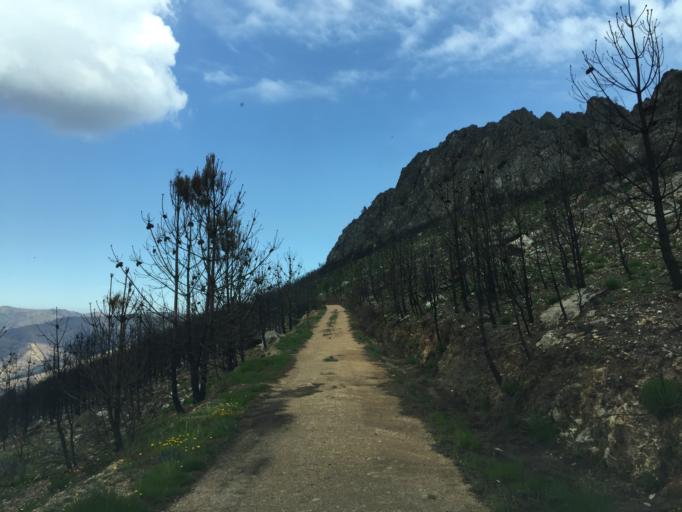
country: PT
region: Coimbra
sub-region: Pampilhosa da Serra
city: Pampilhosa da Serra
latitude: 40.1528
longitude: -7.9278
